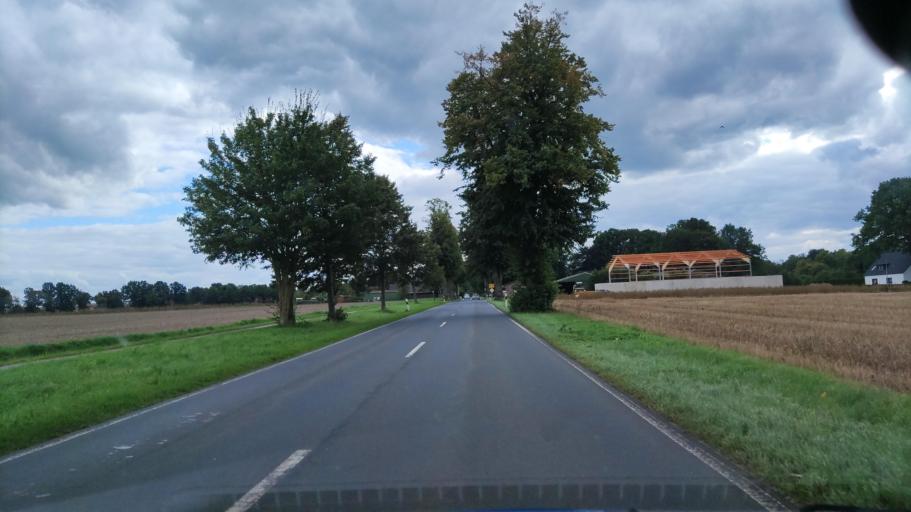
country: DE
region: Lower Saxony
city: Tostedt
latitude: 53.2880
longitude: 9.7131
